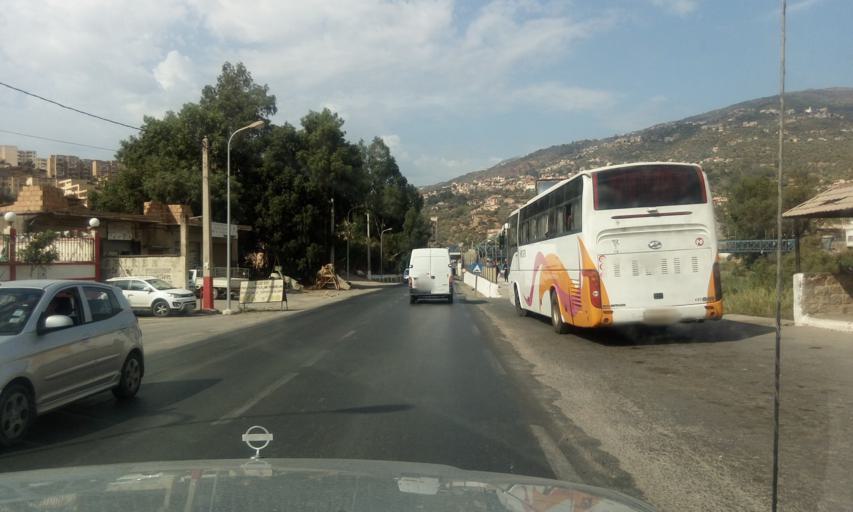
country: DZ
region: Bejaia
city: Seddouk
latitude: 36.6114
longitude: 4.6916
